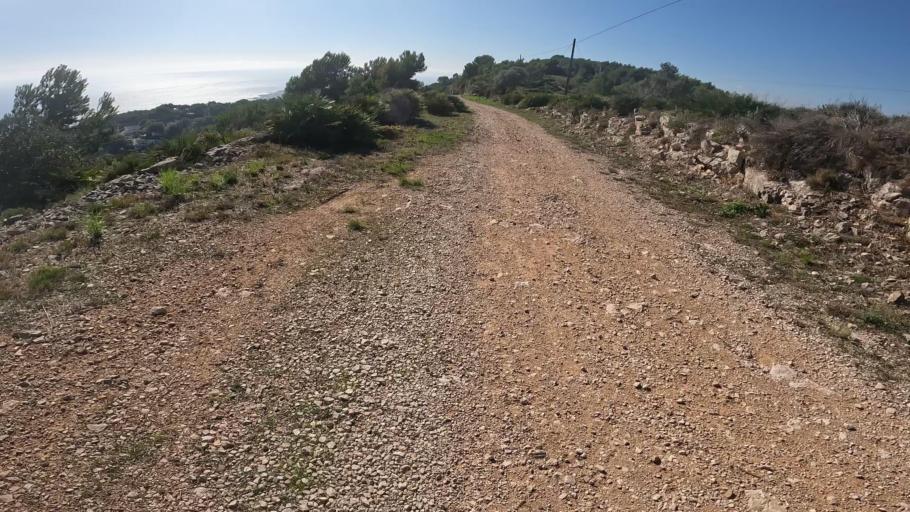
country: ES
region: Valencia
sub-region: Provincia de Castello
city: Alcoceber
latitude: 40.2687
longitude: 0.2734
